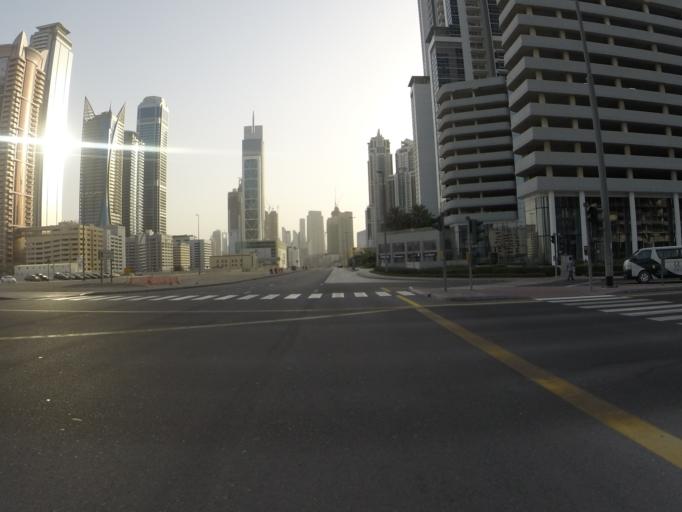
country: AE
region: Dubai
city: Dubai
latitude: 25.1887
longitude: 55.2620
